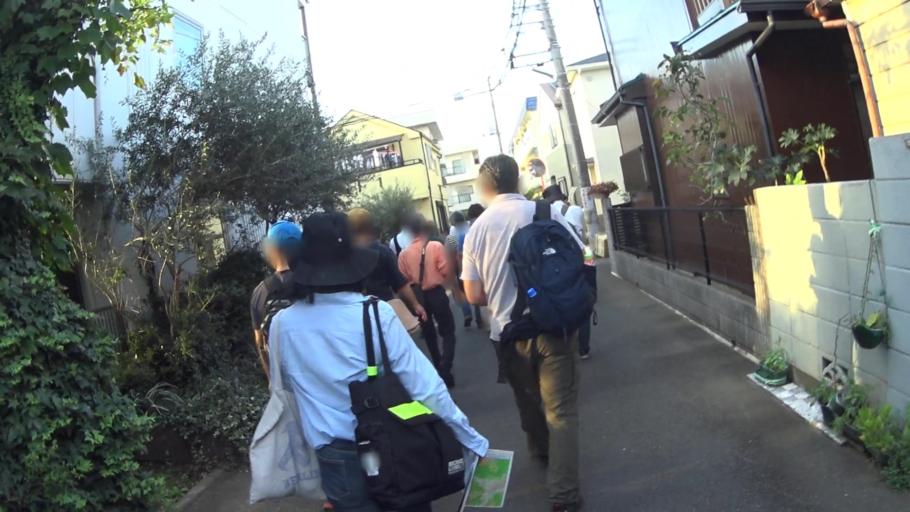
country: JP
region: Tokyo
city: Tanashicho
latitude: 35.7553
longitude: 139.5455
